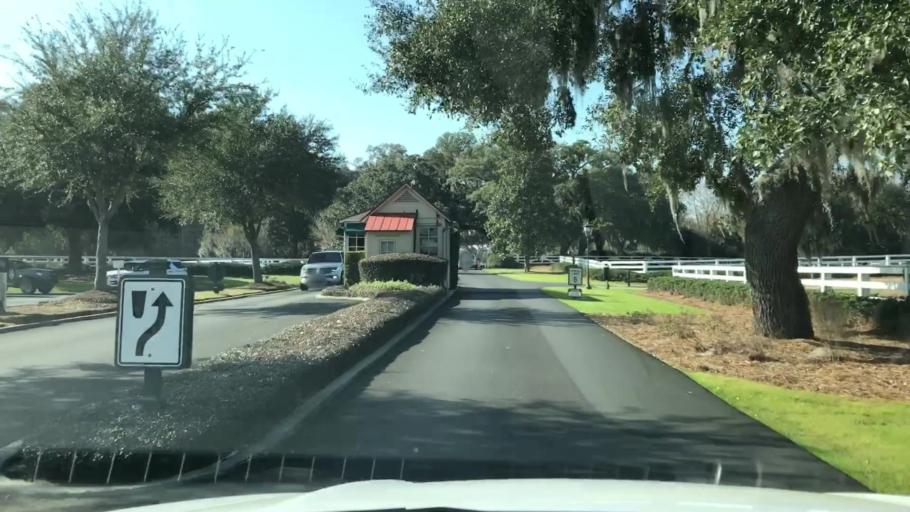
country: US
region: South Carolina
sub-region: Beaufort County
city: Bluffton
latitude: 32.3459
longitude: -80.9248
